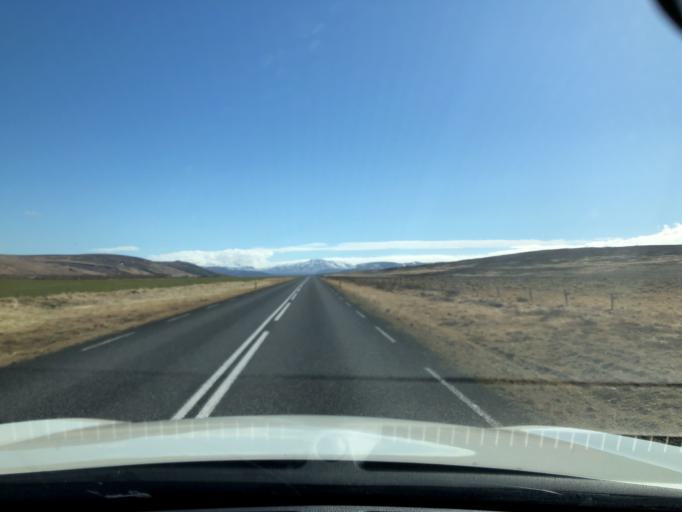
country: IS
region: South
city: Hveragerdi
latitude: 64.7015
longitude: -21.1964
